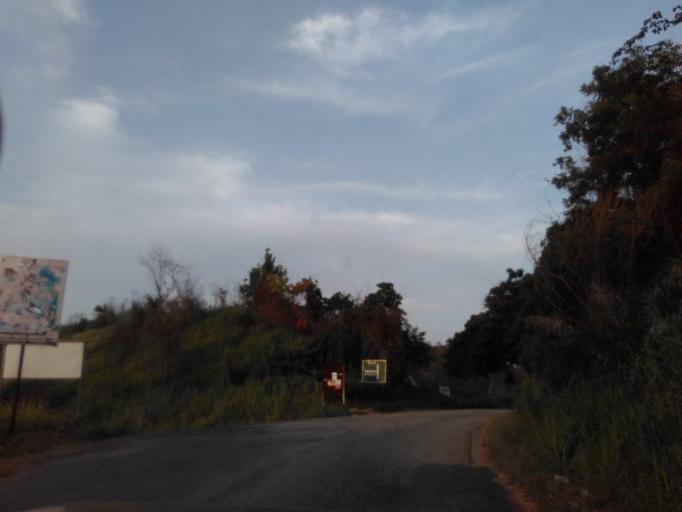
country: GH
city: Bekwai
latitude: 6.5529
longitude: -1.4308
